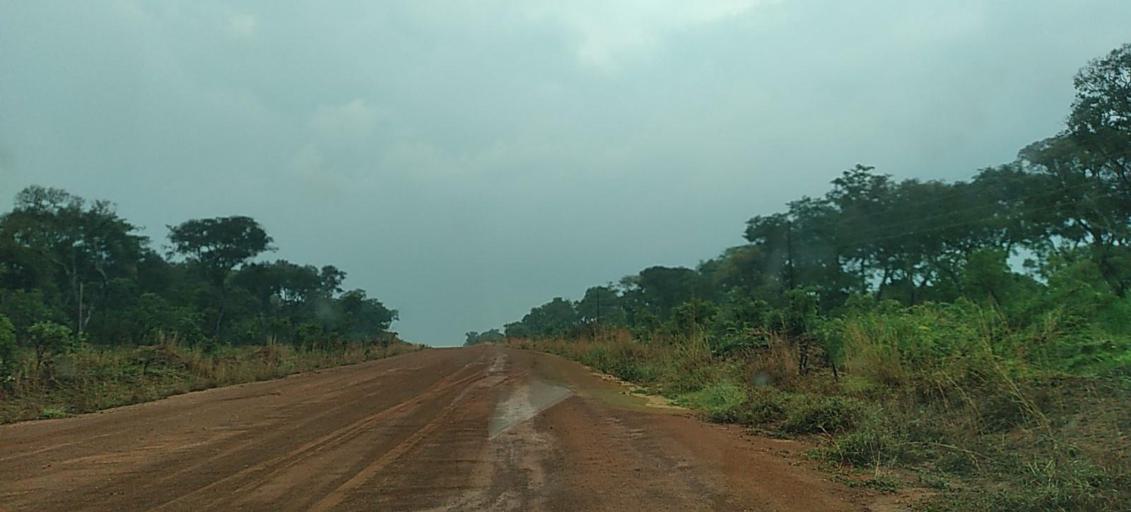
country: ZM
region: North-Western
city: Mwinilunga
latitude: -11.6045
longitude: 24.3950
